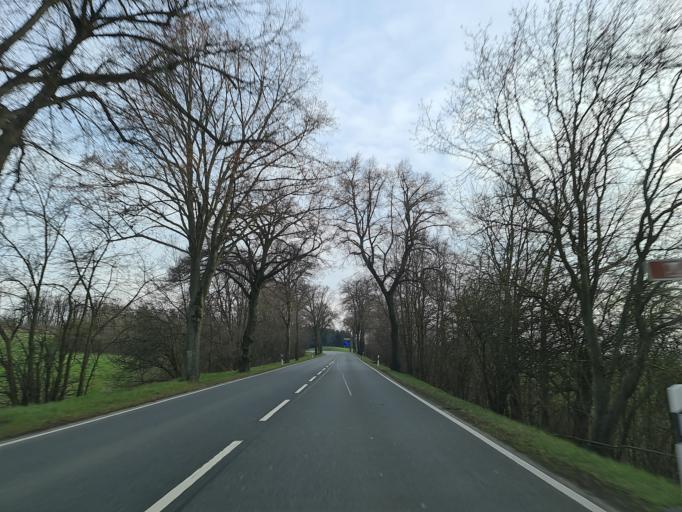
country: DE
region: Saxony
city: Oelsnitz
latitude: 50.4474
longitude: 12.1599
